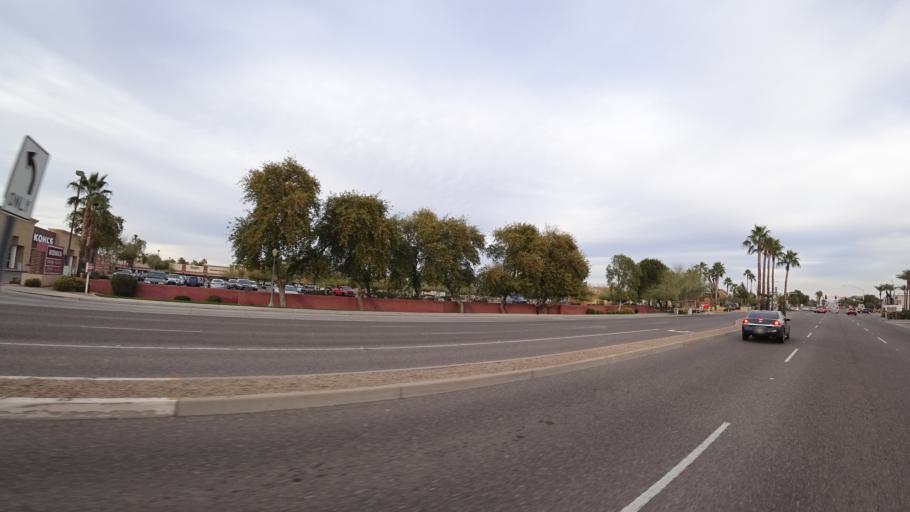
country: US
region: Arizona
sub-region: Maricopa County
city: Surprise
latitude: 33.6386
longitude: -112.3614
